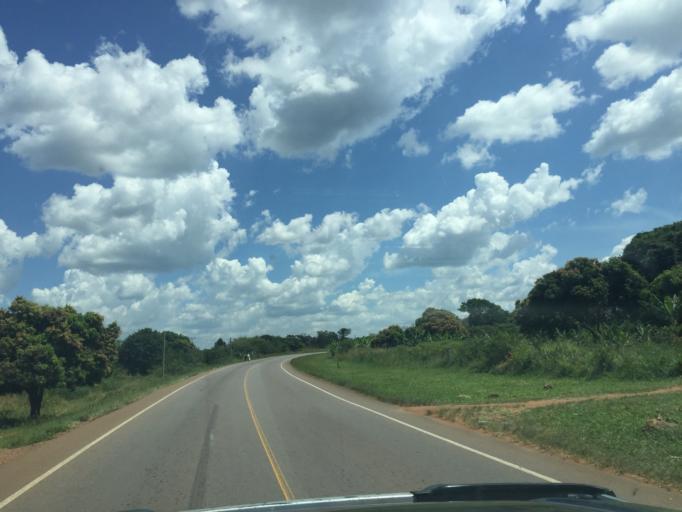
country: UG
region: Central Region
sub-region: Nakasongola District
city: Nakasongola
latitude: 1.3321
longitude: 32.4197
